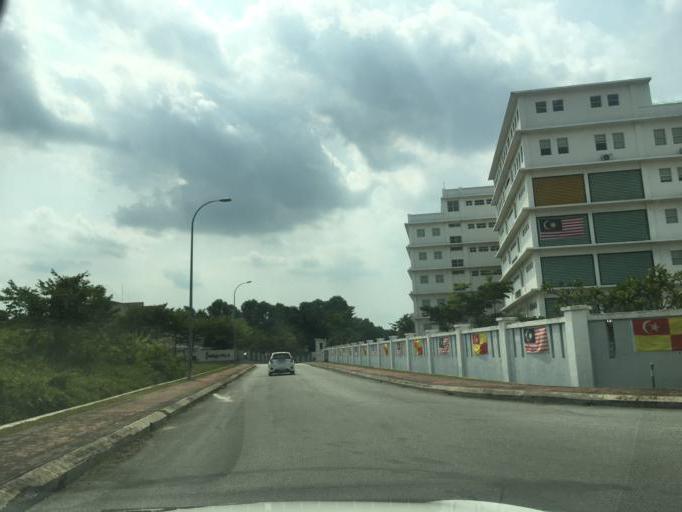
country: MY
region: Selangor
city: Shah Alam
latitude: 3.0781
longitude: 101.4870
